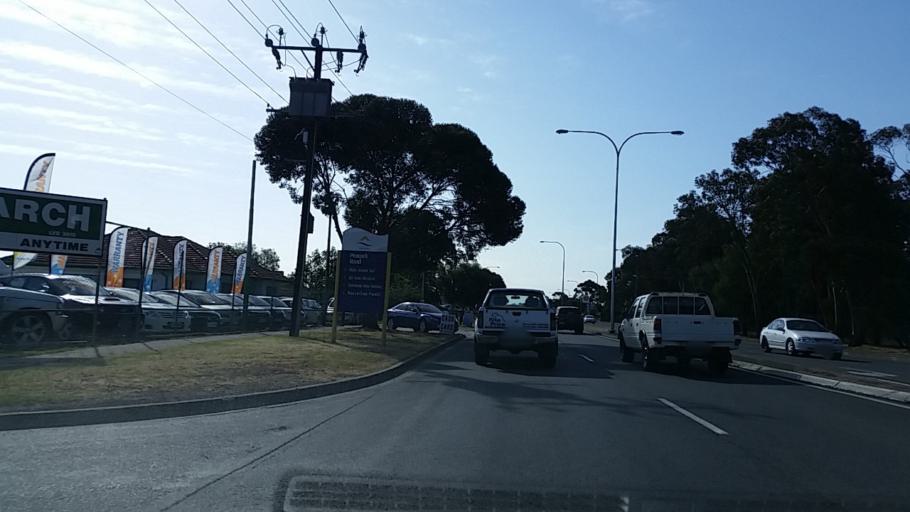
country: AU
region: South Australia
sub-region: Salisbury
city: Salisbury
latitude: -34.7933
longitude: 138.6495
